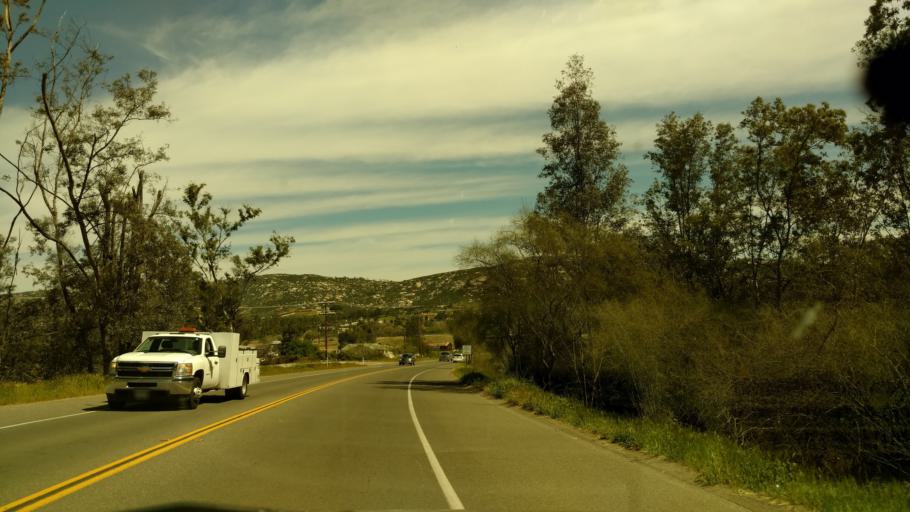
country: US
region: California
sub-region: San Diego County
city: Ramona
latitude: 33.0505
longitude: -116.8544
